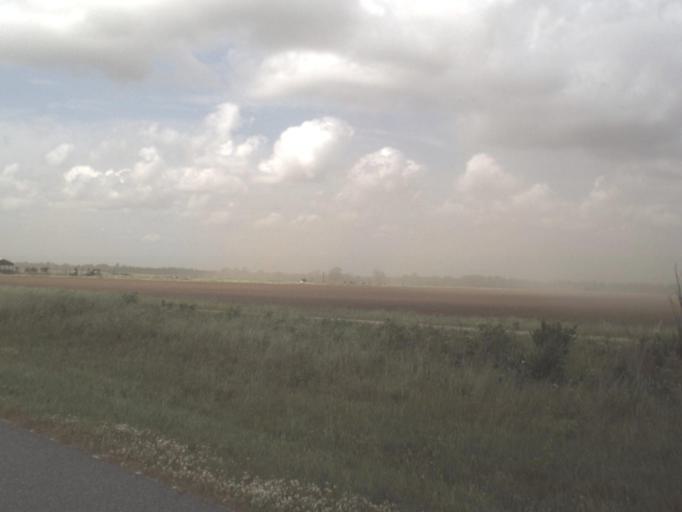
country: US
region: Florida
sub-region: Santa Rosa County
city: Point Baker
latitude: 30.8061
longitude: -87.0986
